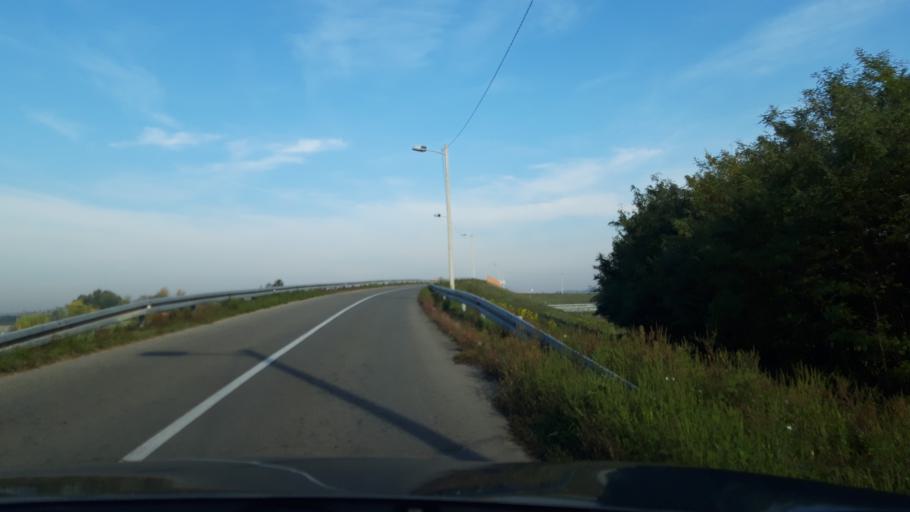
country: HU
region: Csongrad
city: Morahalom
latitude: 46.1270
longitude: 19.8527
